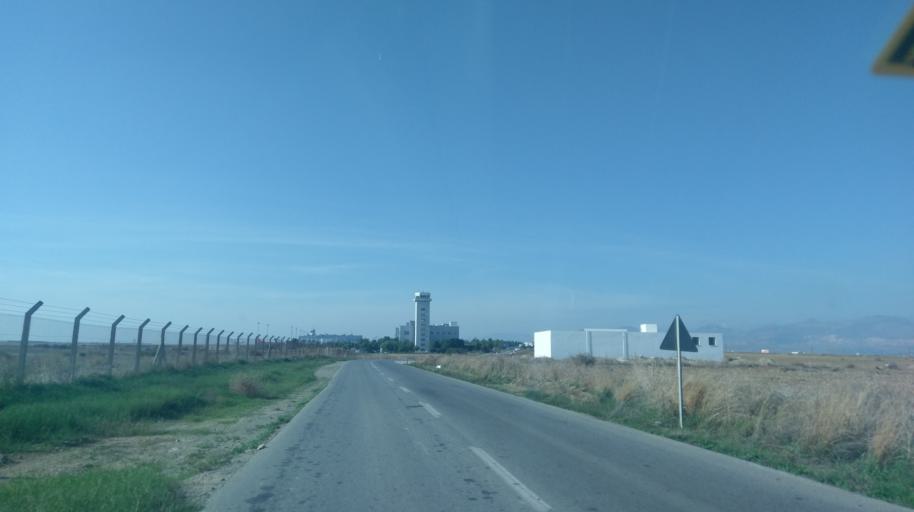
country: CY
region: Larnaka
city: Athienou
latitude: 35.1550
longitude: 33.5121
